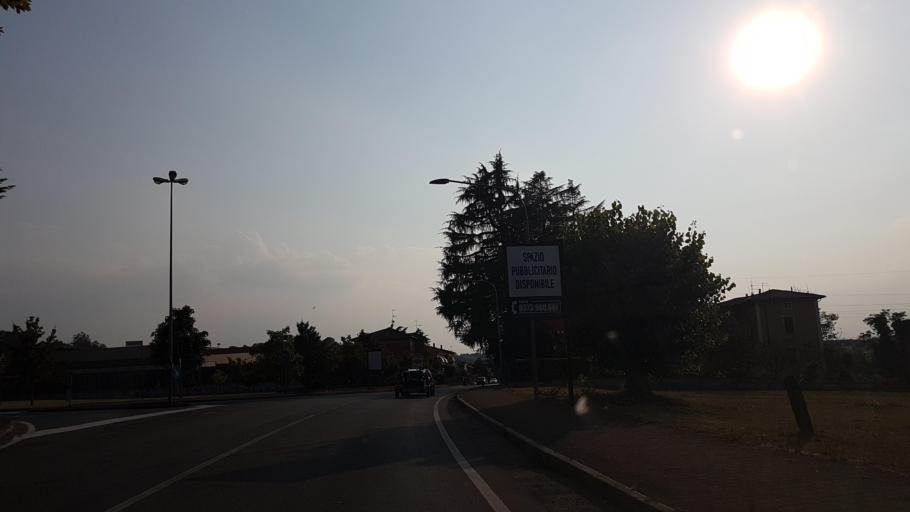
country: IT
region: Emilia-Romagna
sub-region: Provincia di Parma
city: Ozzano Taro
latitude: 44.7096
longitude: 10.1399
